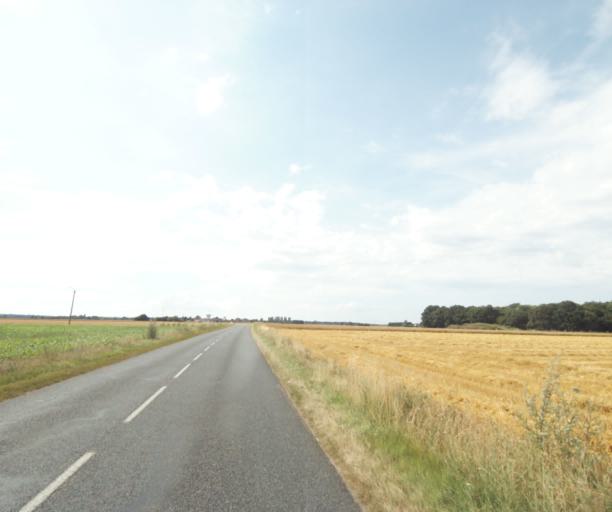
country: FR
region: Ile-de-France
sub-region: Departement de Seine-et-Marne
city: Acheres-la-Foret
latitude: 48.3478
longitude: 2.5851
